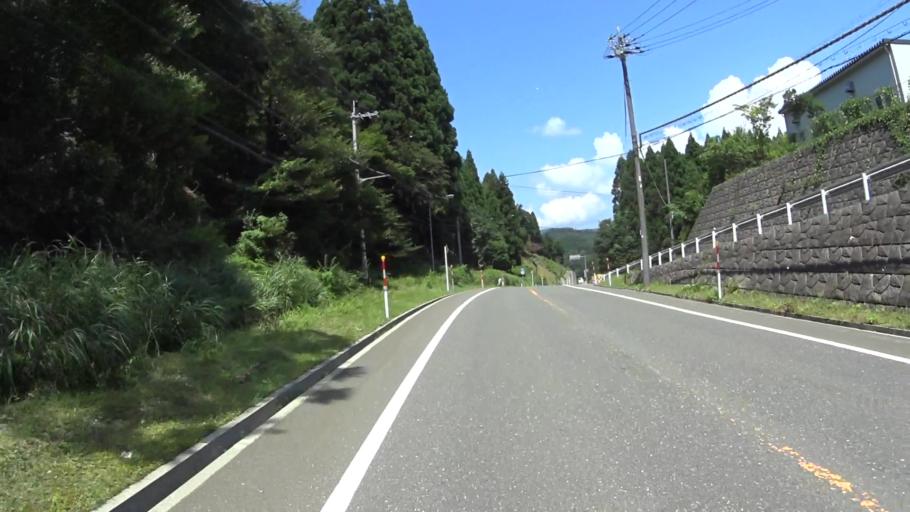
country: JP
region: Fukui
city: Obama
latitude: 35.3945
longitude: 135.9288
